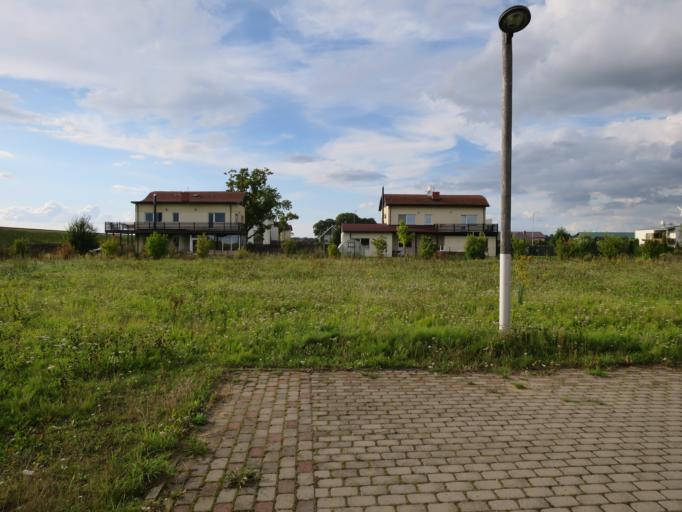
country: LV
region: Ikskile
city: Ikskile
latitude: 56.8347
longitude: 24.4749
